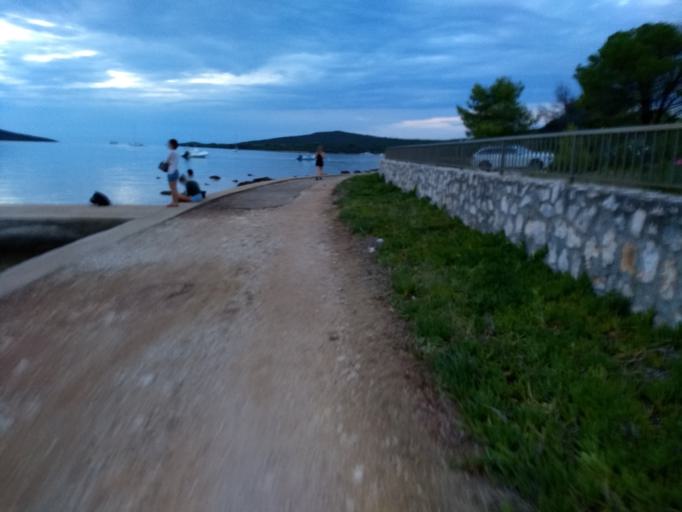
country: HR
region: Zadarska
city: Ugljan
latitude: 44.1358
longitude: 15.0704
